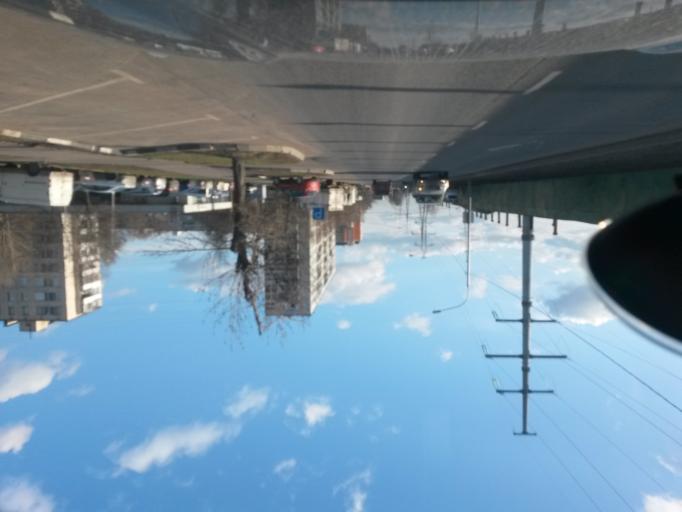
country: RU
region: Moskovskaya
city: Biryulevo Zapadnoye
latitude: 55.5783
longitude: 37.6431
